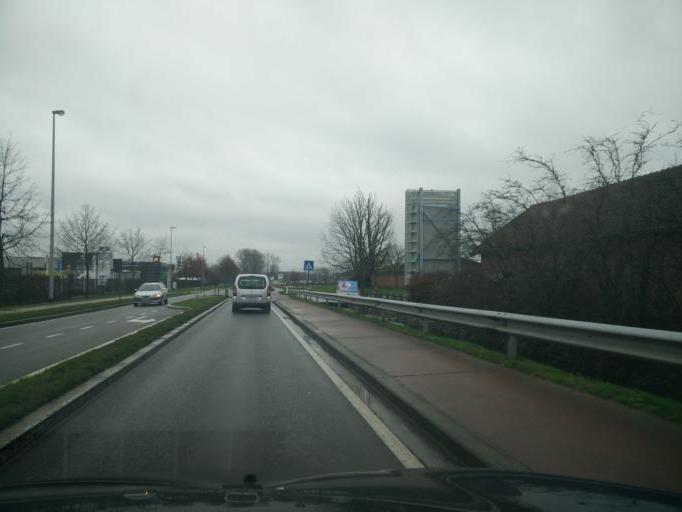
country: BE
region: Flanders
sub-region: Provincie Oost-Vlaanderen
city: Lochristi
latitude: 51.1051
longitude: 3.8693
